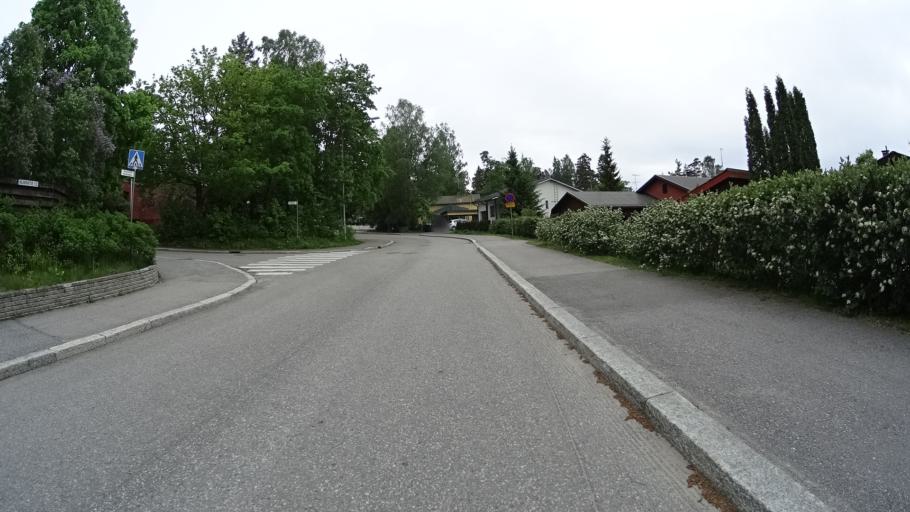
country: FI
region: Uusimaa
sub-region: Helsinki
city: Vantaa
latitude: 60.2668
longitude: 25.0646
